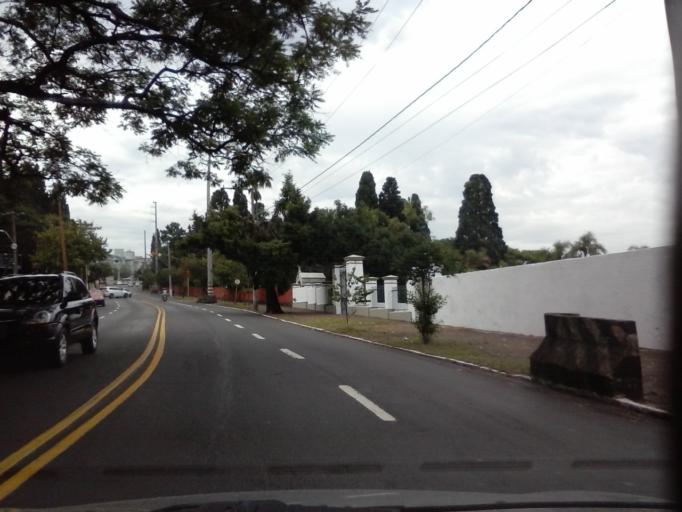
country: BR
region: Rio Grande do Sul
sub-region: Porto Alegre
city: Porto Alegre
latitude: -30.0568
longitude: -51.2102
